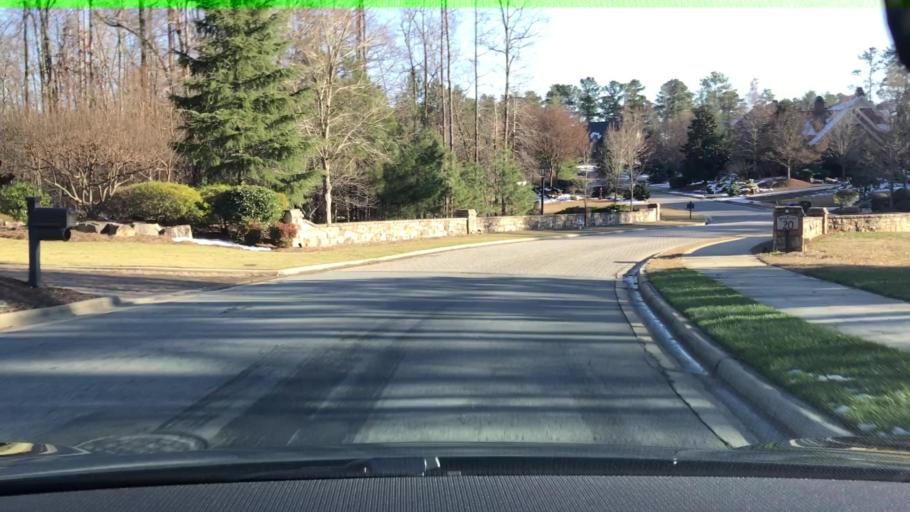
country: US
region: Georgia
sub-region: Gwinnett County
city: Suwanee
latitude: 34.0722
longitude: -84.0968
